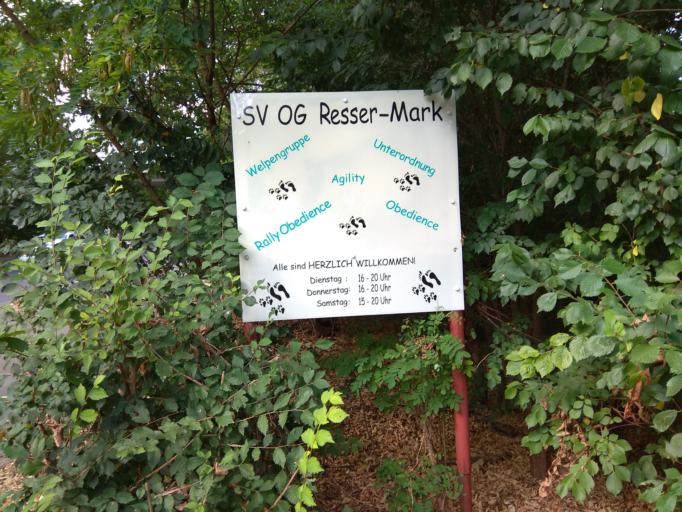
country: DE
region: North Rhine-Westphalia
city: Herten
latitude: 51.5694
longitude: 7.1139
